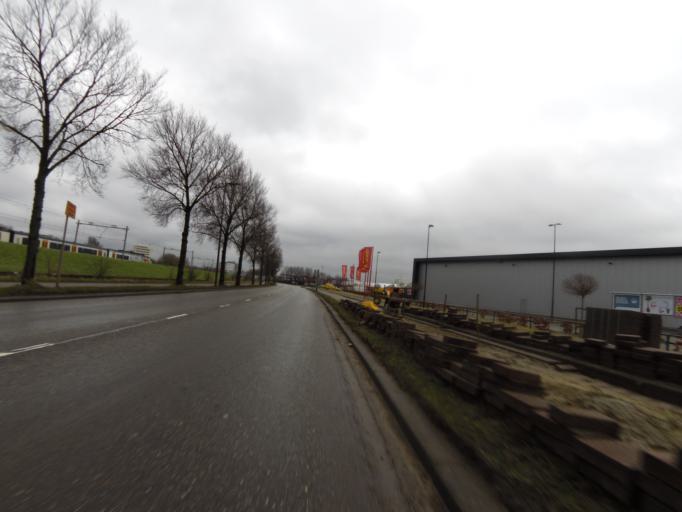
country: NL
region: South Holland
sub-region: Gemeente Vlaardingen
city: Vlaardingen
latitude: 51.9012
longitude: 4.3268
